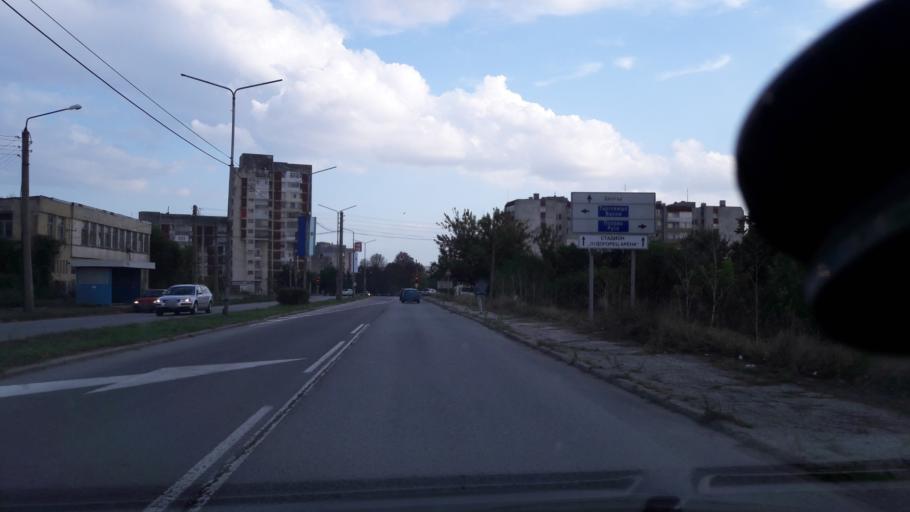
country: BG
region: Razgrad
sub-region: Obshtina Razgrad
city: Razgrad
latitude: 43.5353
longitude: 26.5214
